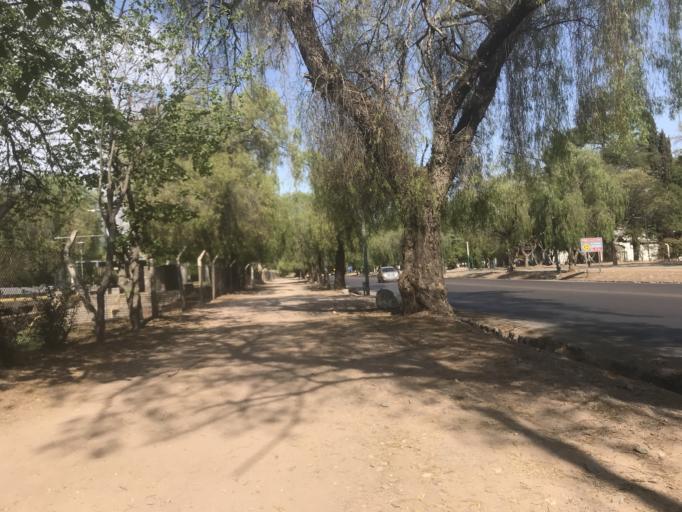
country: AR
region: Mendoza
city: Mendoza
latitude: -32.8837
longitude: -68.8763
